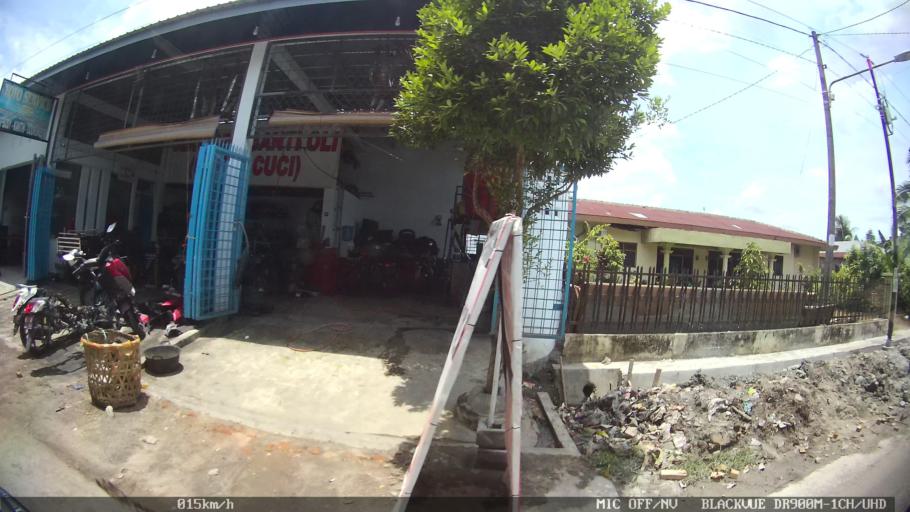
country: ID
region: North Sumatra
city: Percut
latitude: 3.5564
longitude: 98.8685
